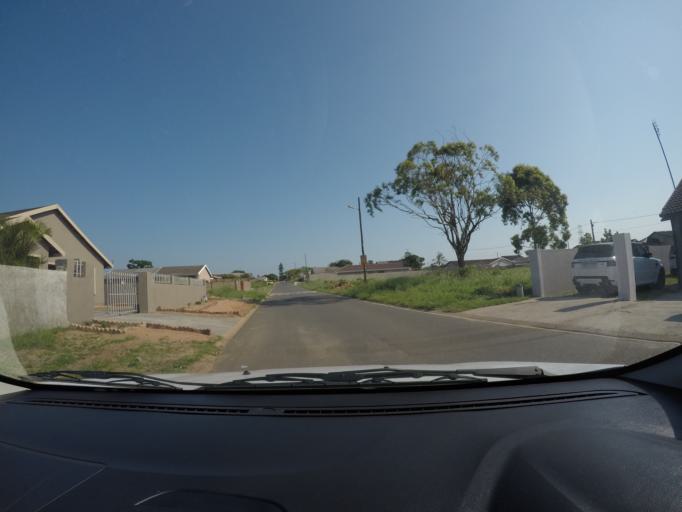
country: ZA
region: KwaZulu-Natal
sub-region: uThungulu District Municipality
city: Richards Bay
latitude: -28.7223
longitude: 32.0369
